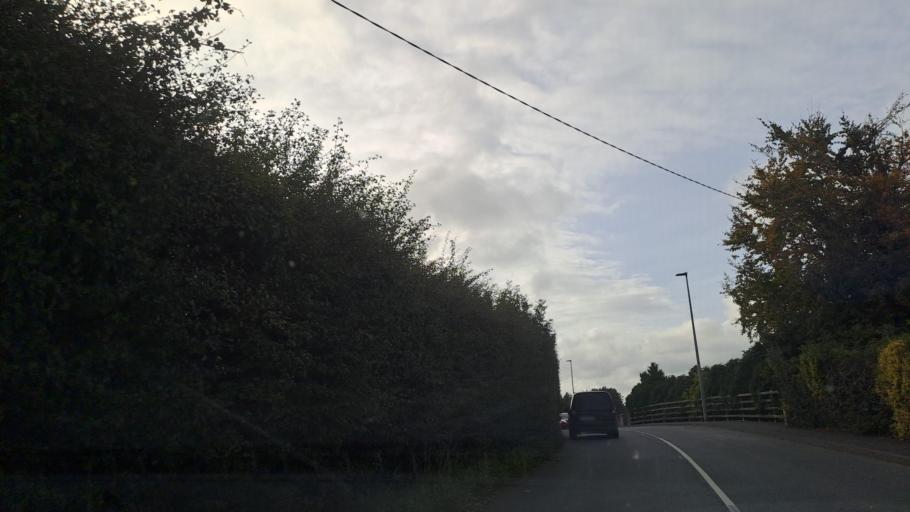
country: IE
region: Ulster
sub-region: An Cabhan
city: Kingscourt
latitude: 53.8236
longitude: -6.7517
